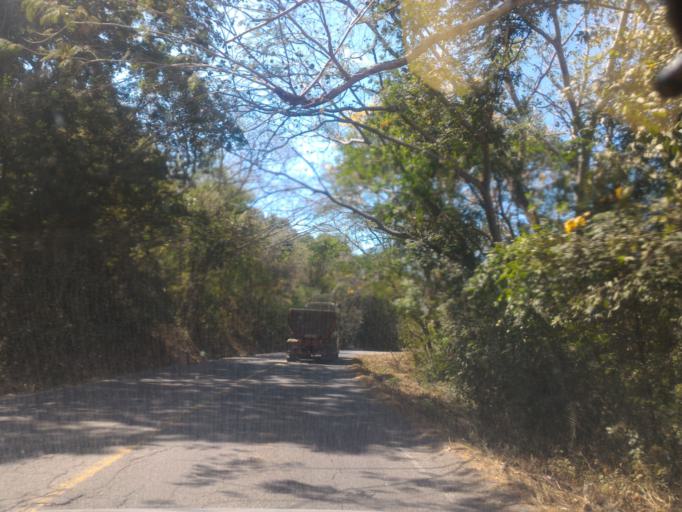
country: MX
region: Michoacan
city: Coahuayana Viejo
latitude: 18.6238
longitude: -103.6747
